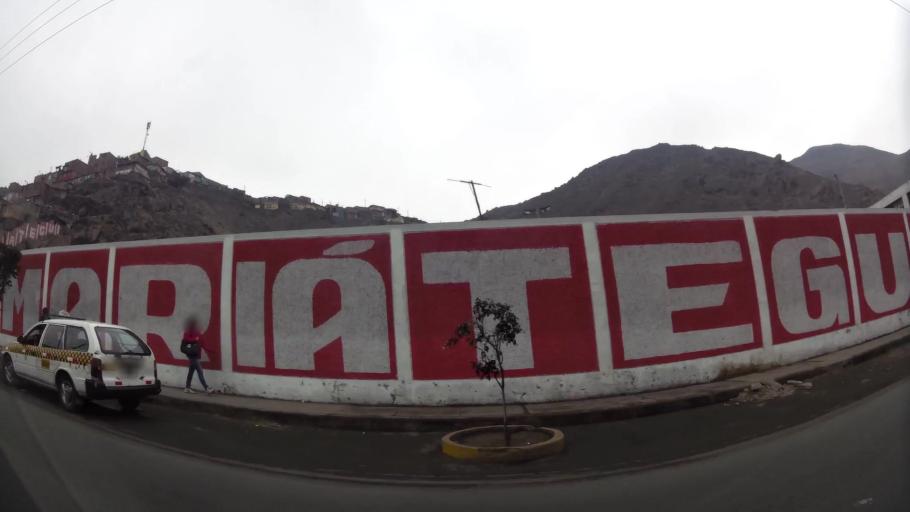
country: PE
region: Lima
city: Lima
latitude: -12.0422
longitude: -76.9975
